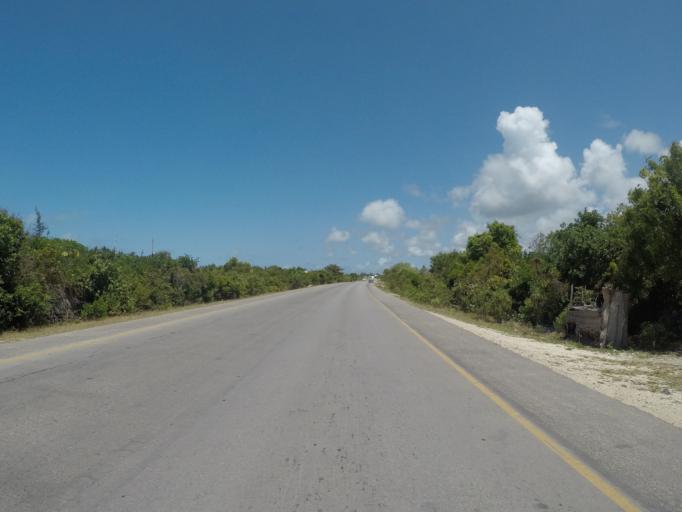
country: TZ
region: Zanzibar Central/South
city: Nganane
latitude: -6.3121
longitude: 39.5416
